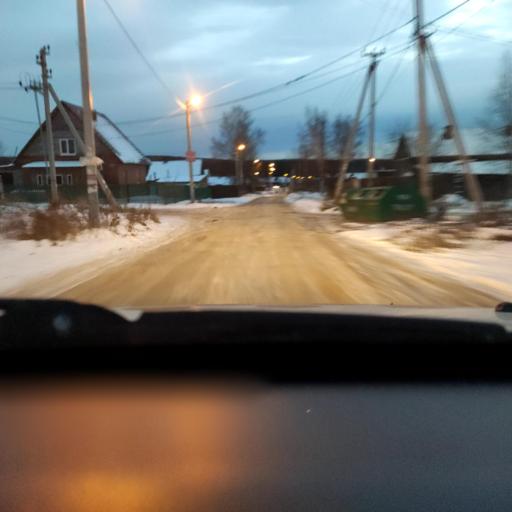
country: RU
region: Perm
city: Perm
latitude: 58.0402
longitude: 56.4001
